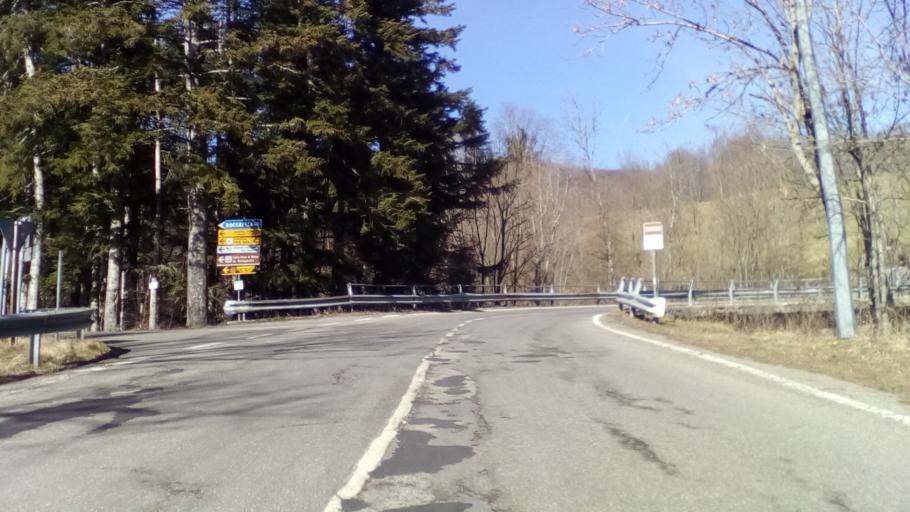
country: IT
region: Emilia-Romagna
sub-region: Provincia di Modena
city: Pievepelago
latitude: 44.2094
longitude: 10.6091
